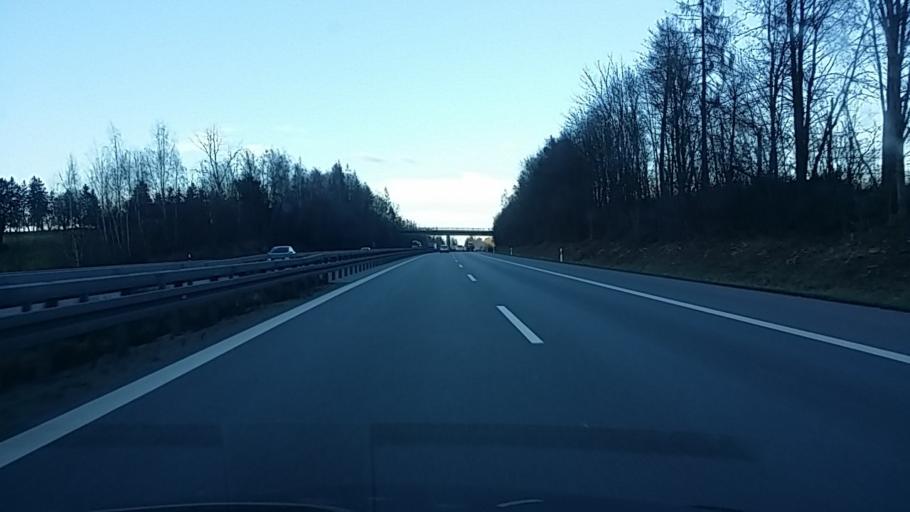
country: DE
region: Bavaria
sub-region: Lower Bavaria
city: Furstenzell
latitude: 48.4831
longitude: 13.3721
